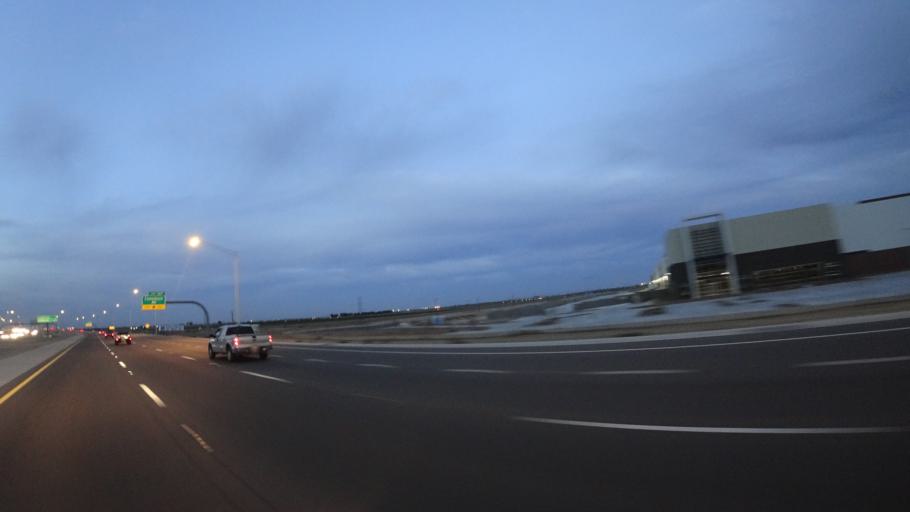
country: US
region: Arizona
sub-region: Maricopa County
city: Citrus Park
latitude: 33.4990
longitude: -112.4192
